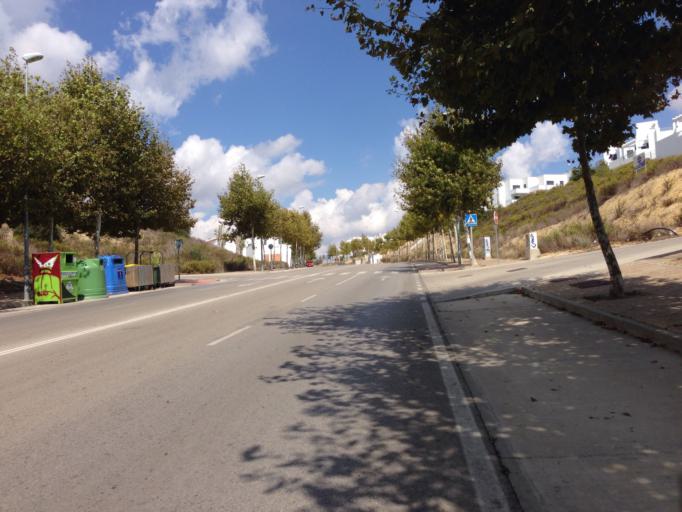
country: ES
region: Andalusia
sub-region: Provincia de Cadiz
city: Conil de la Frontera
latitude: 36.2788
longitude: -6.0792
